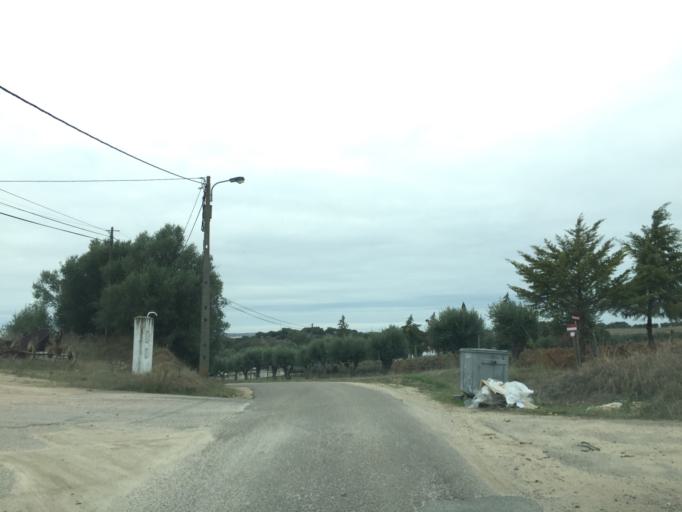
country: PT
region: Portalegre
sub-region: Fronteira
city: Vale da Amoreira
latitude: 39.0509
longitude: -7.7662
